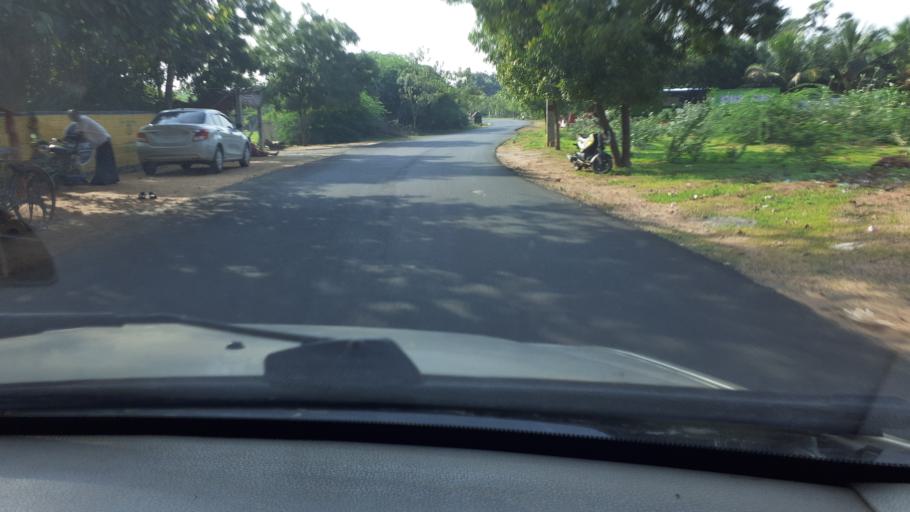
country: IN
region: Tamil Nadu
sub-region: Thoothukkudi
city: Eral
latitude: 8.5785
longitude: 78.0264
